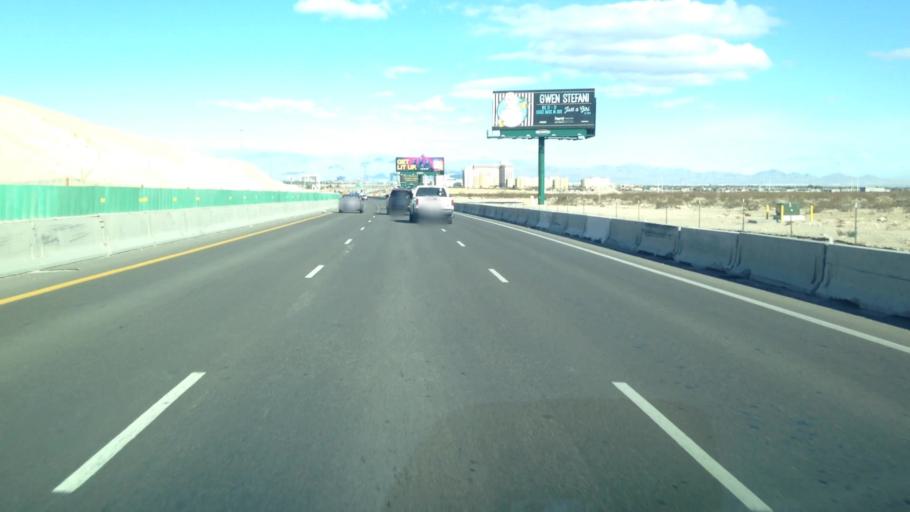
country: US
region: Nevada
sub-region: Clark County
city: Enterprise
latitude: 35.9849
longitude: -115.1803
